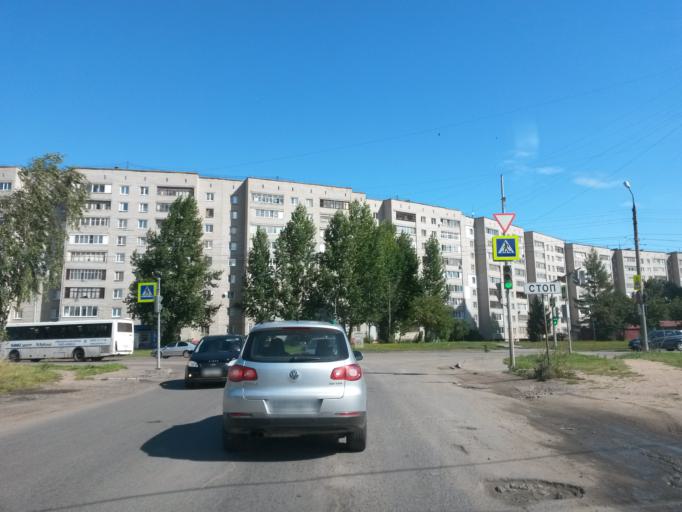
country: RU
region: Jaroslavl
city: Yaroslavl
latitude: 57.5695
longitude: 39.8609
